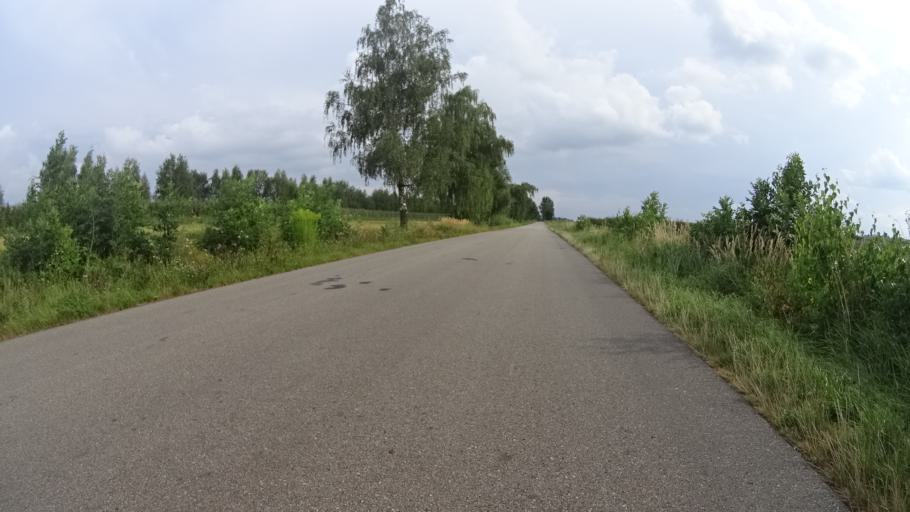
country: PL
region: Masovian Voivodeship
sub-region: Powiat grojecki
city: Goszczyn
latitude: 51.6990
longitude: 20.8556
